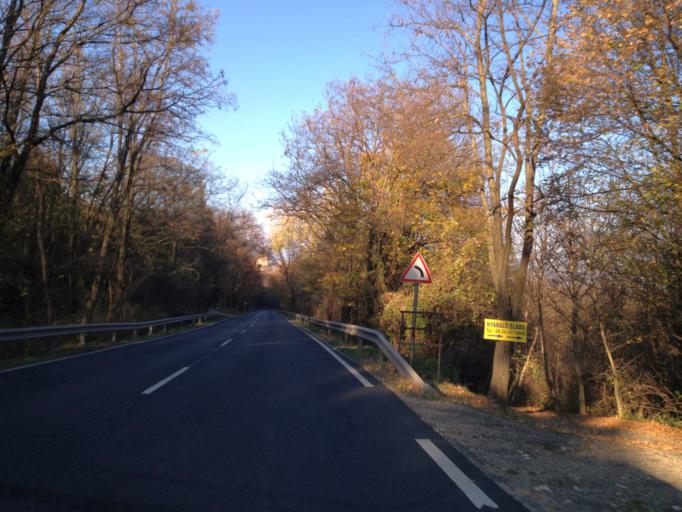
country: HU
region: Veszprem
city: Zirc
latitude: 47.3435
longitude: 17.8791
